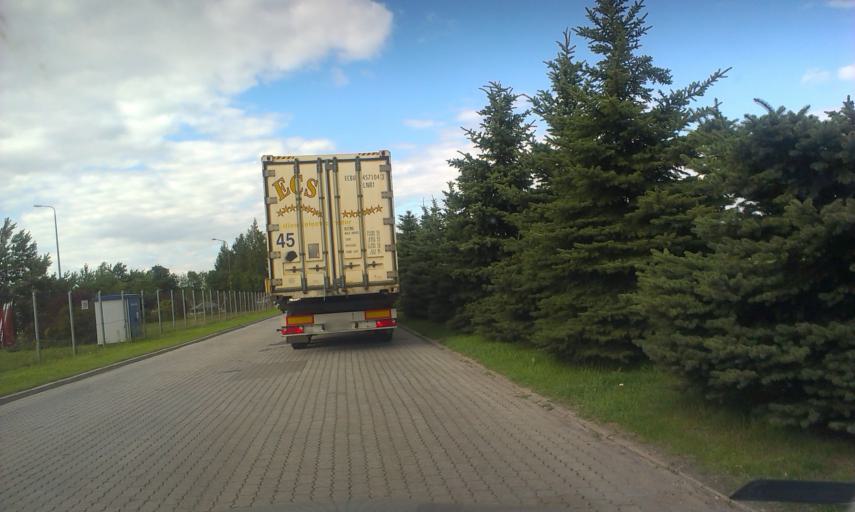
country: PL
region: Masovian Voivodeship
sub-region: Powiat zyrardowski
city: Mszczonow
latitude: 51.9722
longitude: 20.5475
